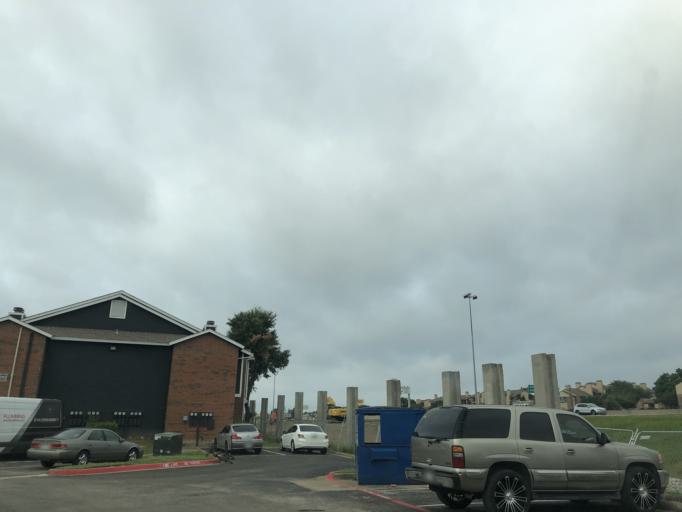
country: US
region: Texas
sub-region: Dallas County
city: Garland
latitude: 32.8401
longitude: -96.6324
